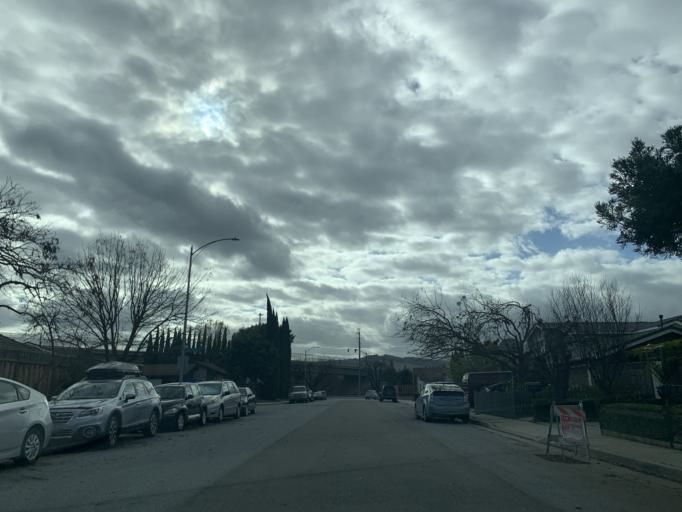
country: US
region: California
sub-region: Santa Clara County
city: Seven Trees
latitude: 37.2425
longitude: -121.7779
